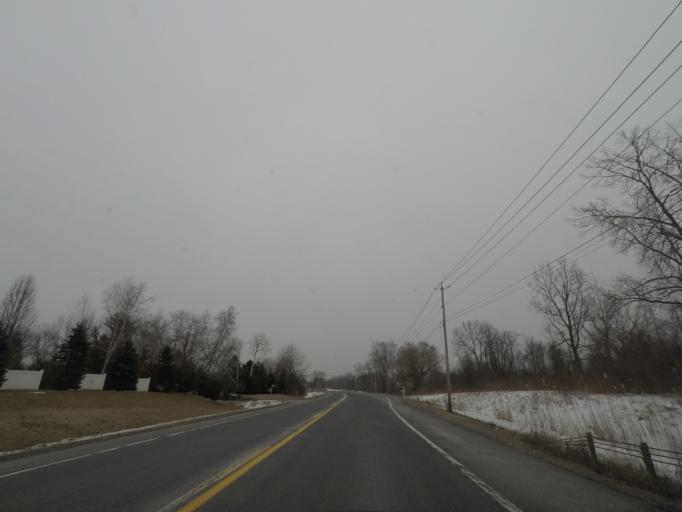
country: US
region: New York
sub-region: Albany County
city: Delmar
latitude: 42.5660
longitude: -73.8437
